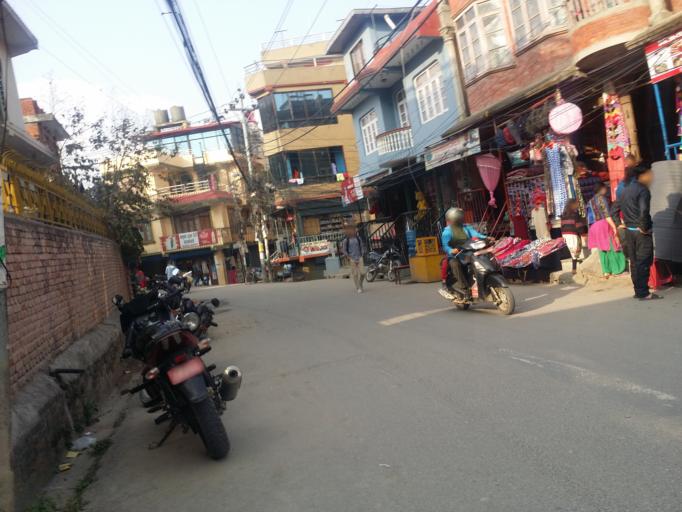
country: NP
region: Central Region
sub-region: Bagmati Zone
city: Kathmandu
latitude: 27.7019
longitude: 85.3469
